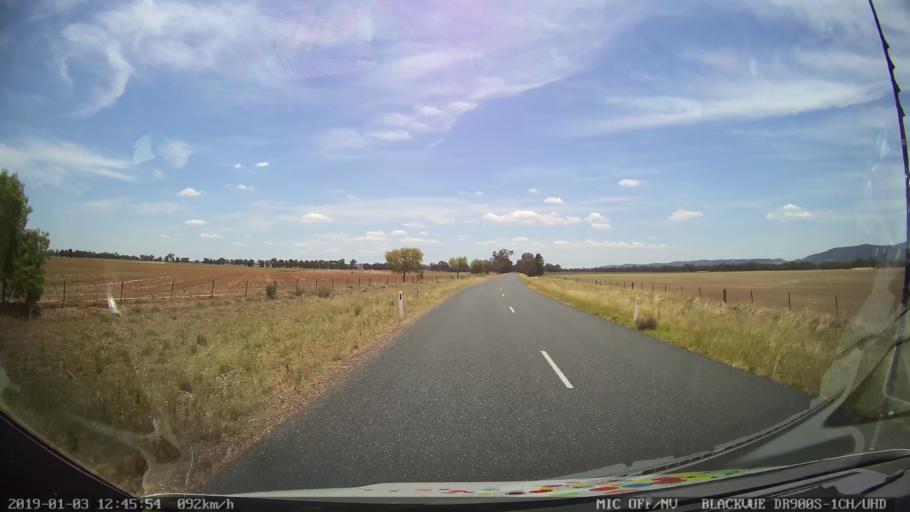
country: AU
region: New South Wales
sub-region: Weddin
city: Grenfell
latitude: -33.7438
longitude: 148.2272
